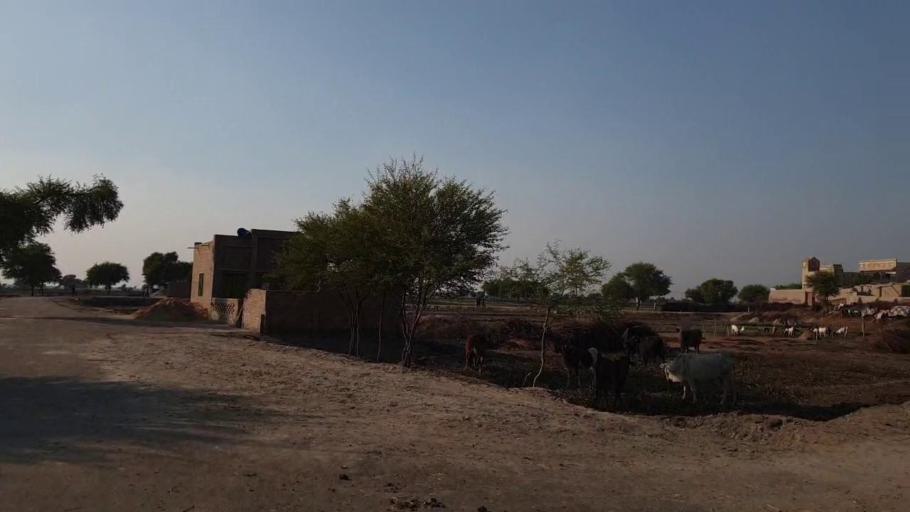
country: PK
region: Sindh
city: Sehwan
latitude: 26.4270
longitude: 67.7853
